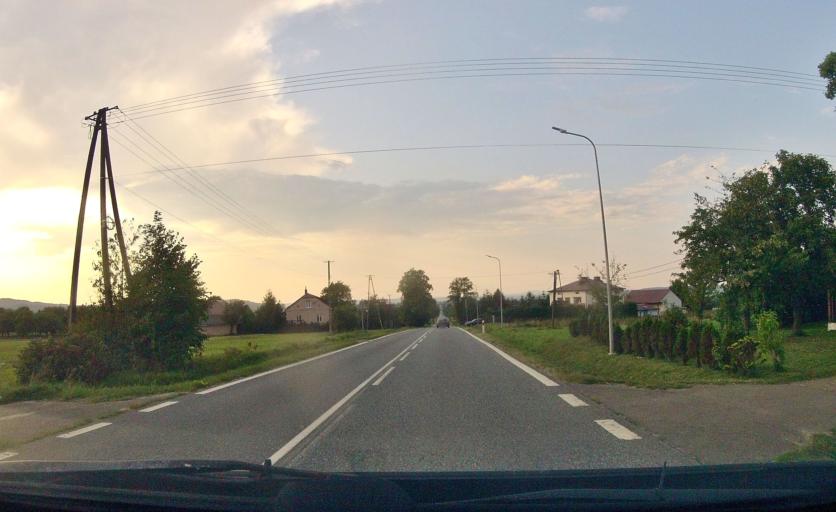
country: PL
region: Subcarpathian Voivodeship
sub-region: Powiat jasielski
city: Nowy Zmigrod
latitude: 49.5875
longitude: 21.5448
